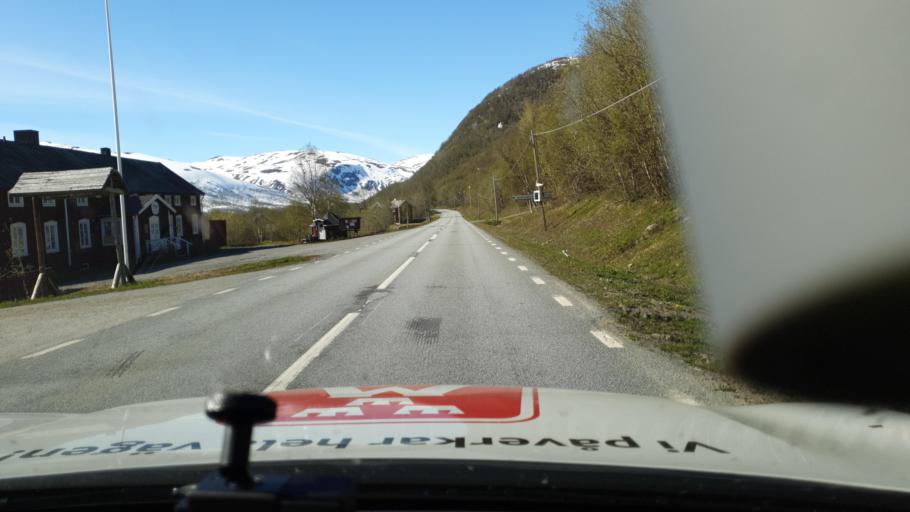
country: NO
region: Nordland
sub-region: Rana
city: Mo i Rana
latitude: 65.8678
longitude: 15.0159
